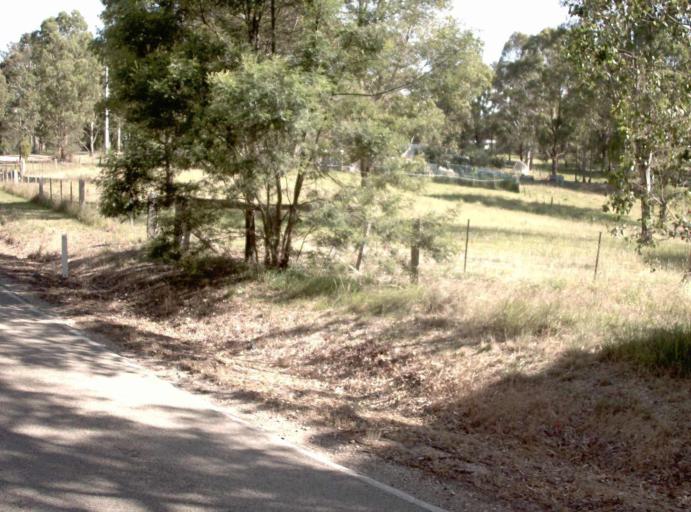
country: AU
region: Victoria
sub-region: East Gippsland
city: Lakes Entrance
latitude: -37.7727
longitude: 147.8138
